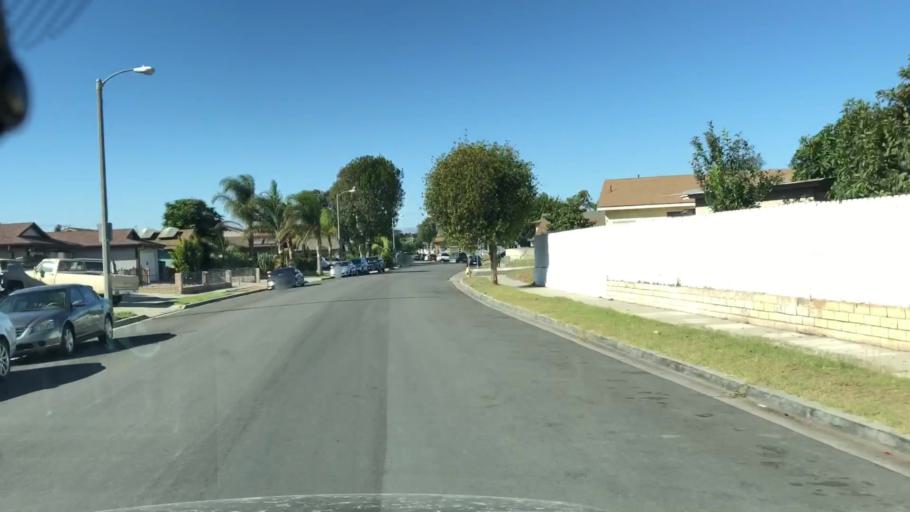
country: US
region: California
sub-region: Ventura County
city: Oxnard
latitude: 34.1697
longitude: -119.1664
